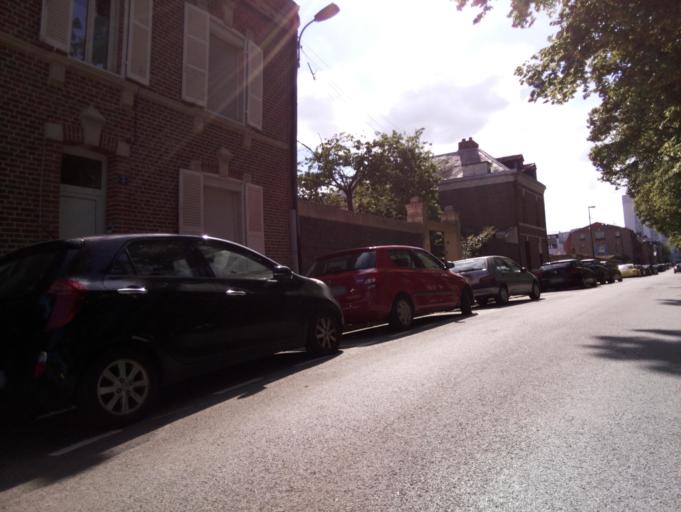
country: FR
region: Picardie
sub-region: Departement de la Somme
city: Amiens
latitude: 49.8969
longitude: 2.2824
